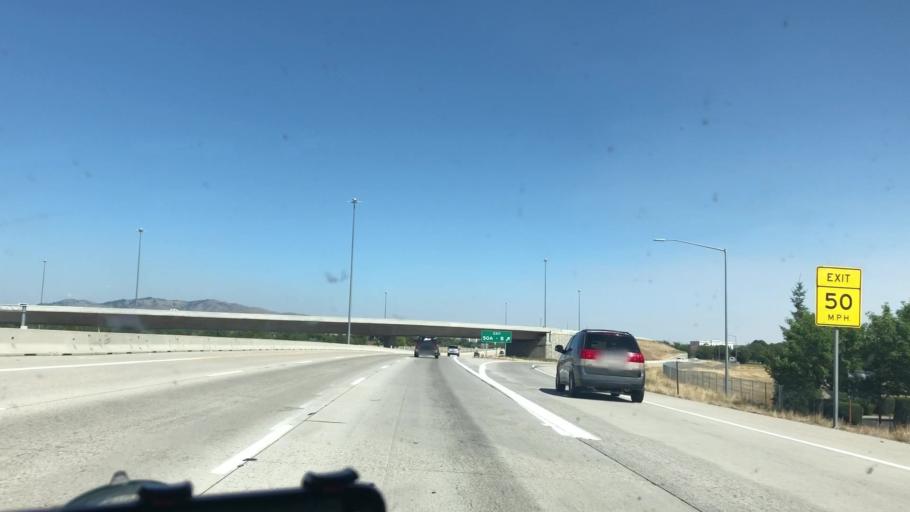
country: US
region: Idaho
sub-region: Ada County
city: Garden City
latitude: 43.5968
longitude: -116.2923
